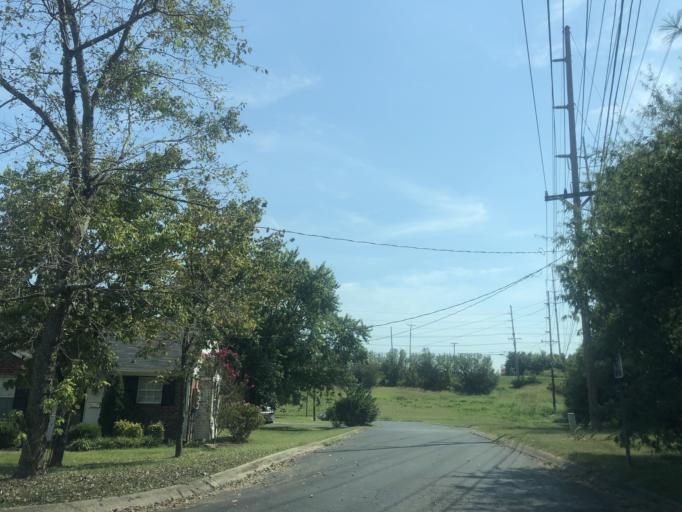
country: US
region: Tennessee
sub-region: Williamson County
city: Brentwood Estates
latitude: 36.0474
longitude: -86.7093
